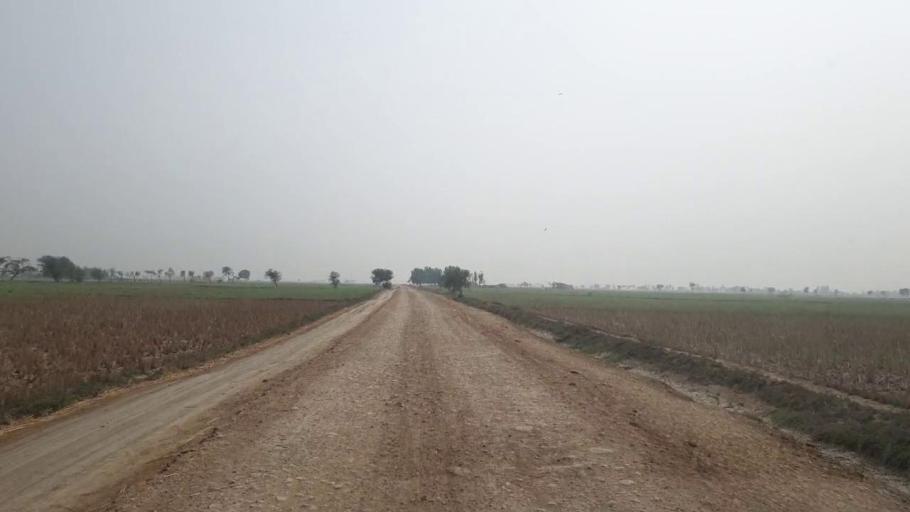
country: PK
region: Sindh
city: Kario
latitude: 24.6447
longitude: 68.5954
